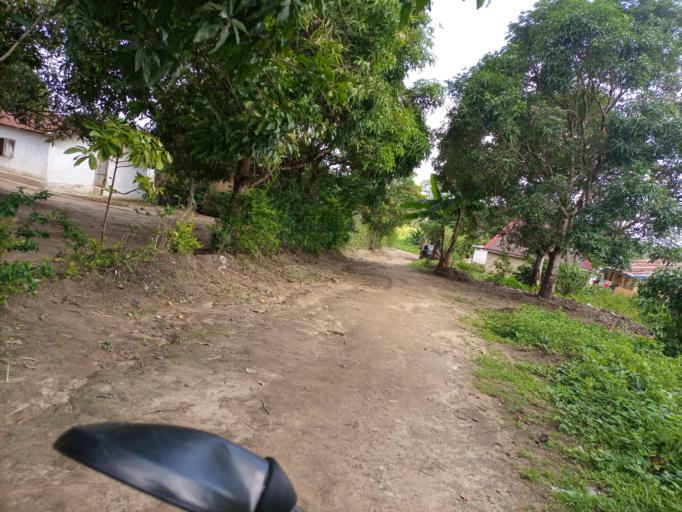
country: SL
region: Southern Province
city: Bo
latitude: 7.9665
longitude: -11.7665
